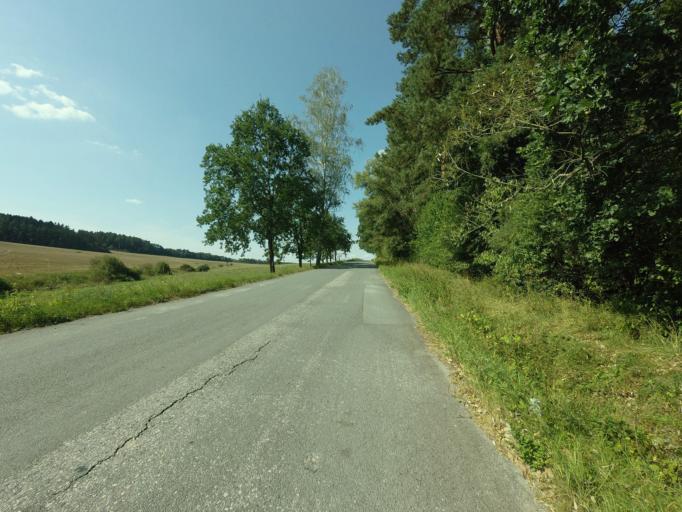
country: CZ
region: Jihocesky
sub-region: Okres Ceske Budejovice
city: Hluboka nad Vltavou
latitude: 49.1390
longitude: 14.4482
